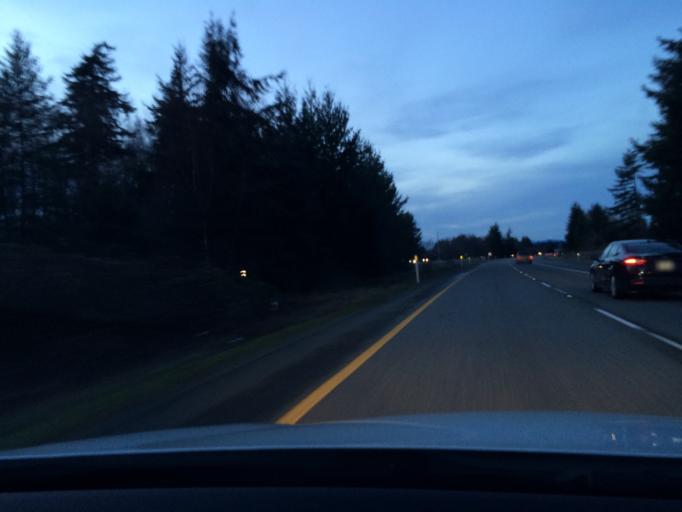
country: US
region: Washington
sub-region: Whatcom County
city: Ferndale
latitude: 48.9107
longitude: -122.6255
